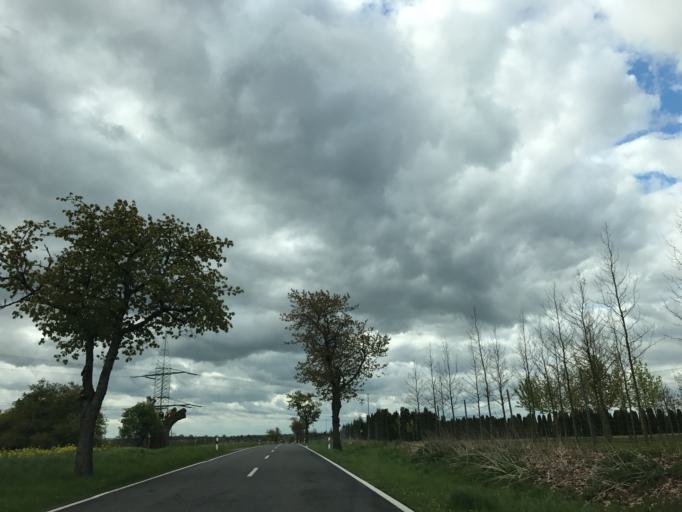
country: DE
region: Brandenburg
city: Pawesin
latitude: 52.5615
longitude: 12.7686
